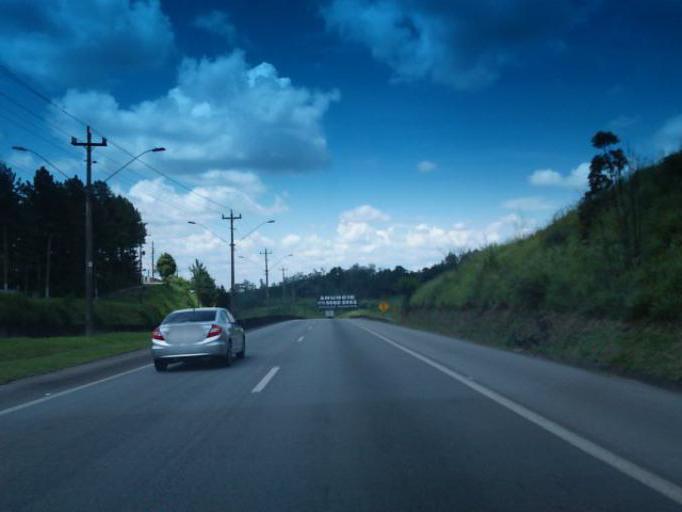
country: BR
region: Sao Paulo
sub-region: Sao Lourenco Da Serra
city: Sao Lourenco da Serra
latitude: -23.8314
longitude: -46.9287
